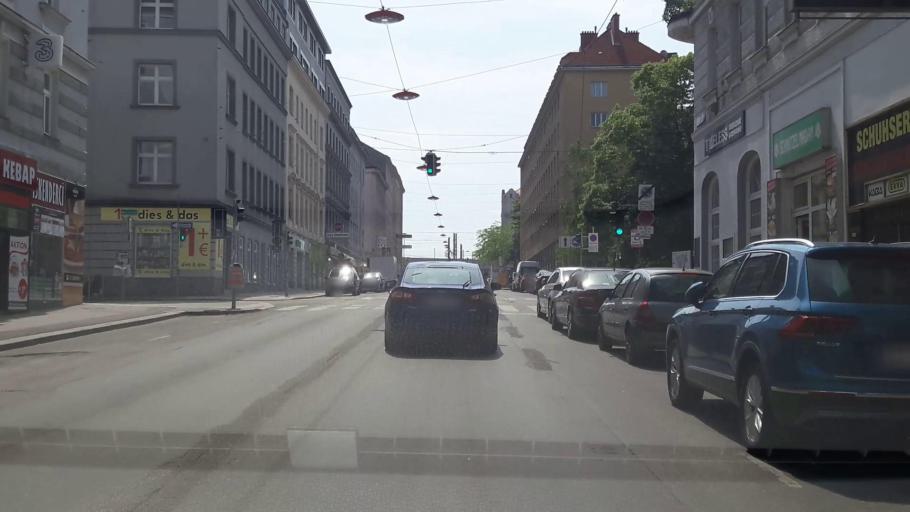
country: AT
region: Vienna
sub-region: Wien Stadt
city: Vienna
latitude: 48.1832
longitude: 16.3564
